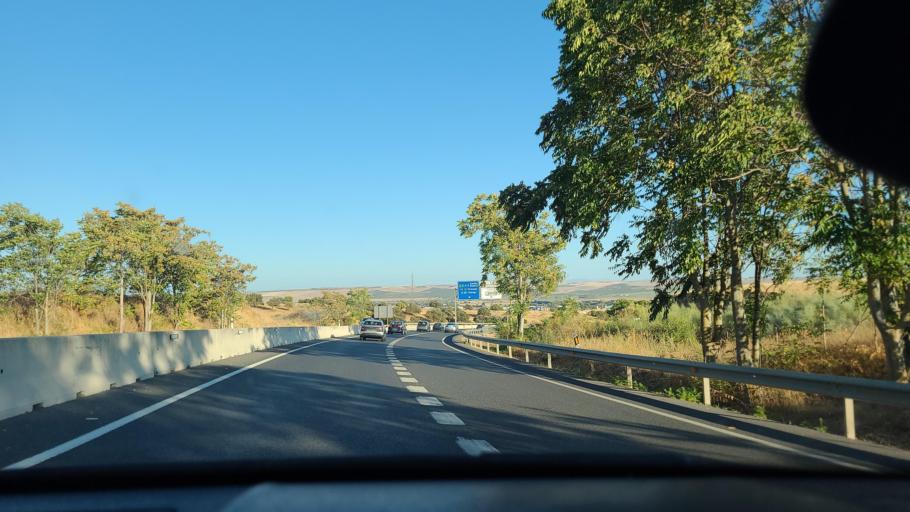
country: ES
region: Andalusia
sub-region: Province of Cordoba
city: Cordoba
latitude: 37.9137
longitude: -4.7551
